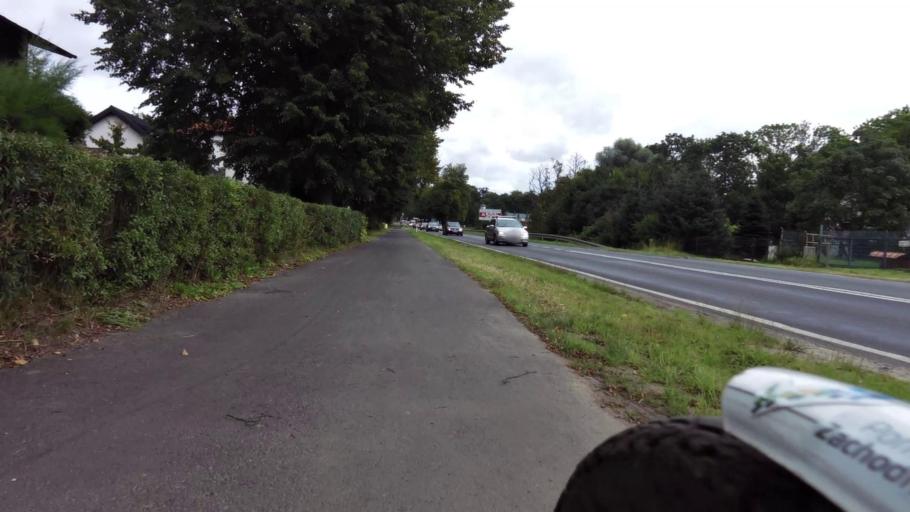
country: PL
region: West Pomeranian Voivodeship
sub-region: Powiat koszalinski
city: Mielno
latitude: 54.2174
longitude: 16.1092
